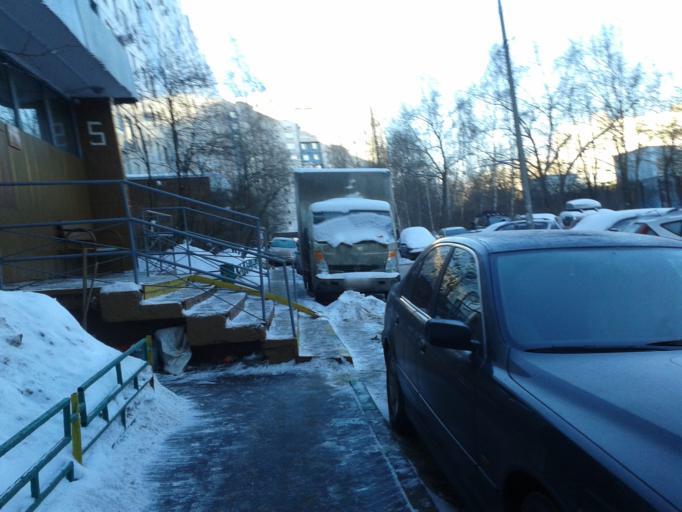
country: RU
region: Moscow
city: Strogino
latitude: 55.8043
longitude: 37.4070
